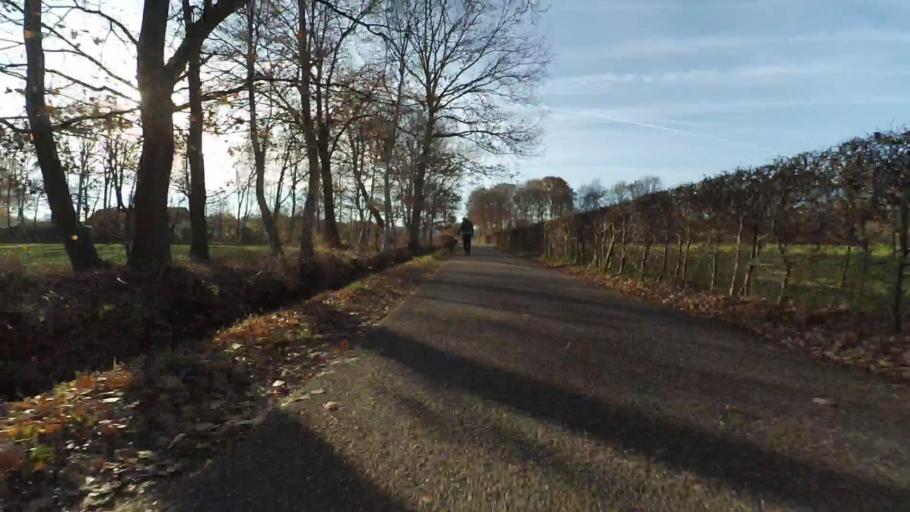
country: NL
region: Utrecht
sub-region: Gemeente Veenendaal
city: Veenendaal
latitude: 52.0200
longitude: 5.5247
